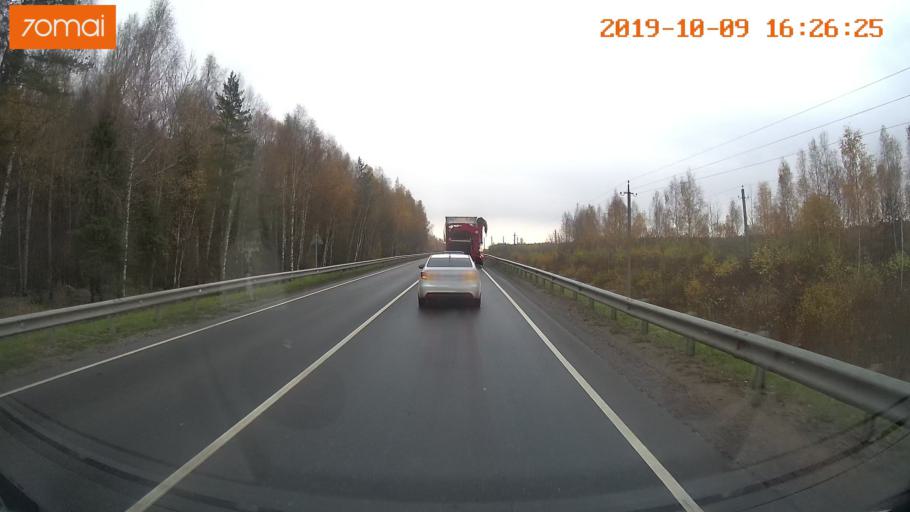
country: RU
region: Kostroma
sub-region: Kostromskoy Rayon
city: Kostroma
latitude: 57.6377
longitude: 40.9240
